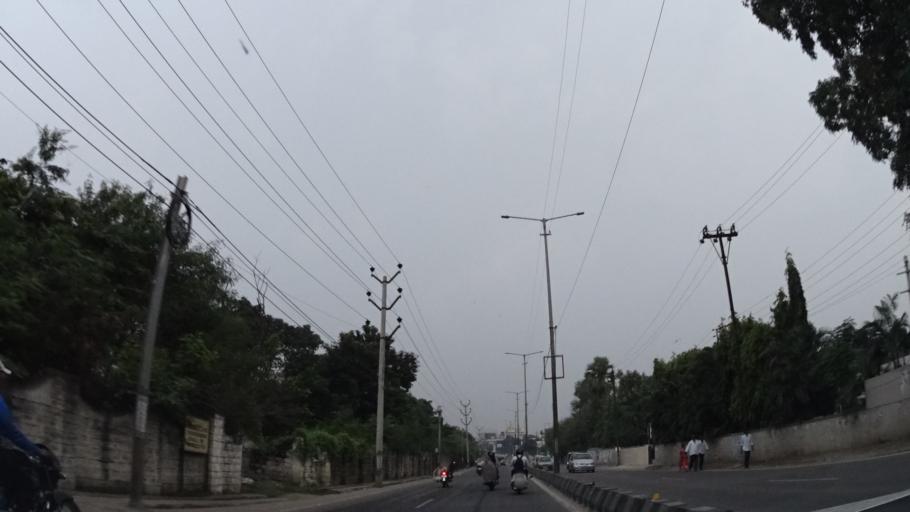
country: IN
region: Telangana
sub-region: Hyderabad
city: Malkajgiri
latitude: 17.4482
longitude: 78.4875
